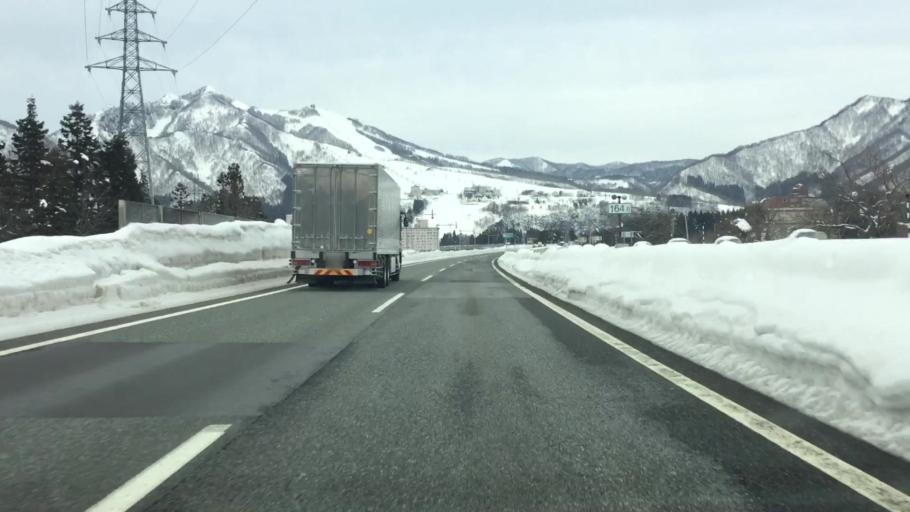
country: JP
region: Niigata
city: Shiozawa
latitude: 36.9165
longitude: 138.8397
